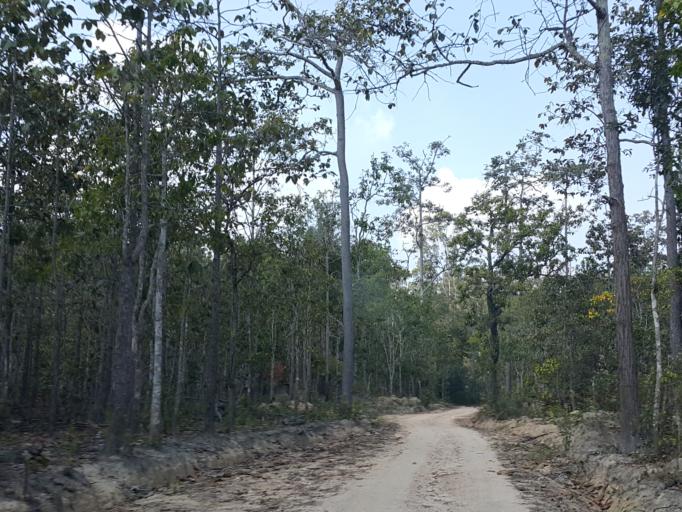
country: TH
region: Chiang Mai
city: Hot
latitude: 18.1341
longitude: 98.4272
